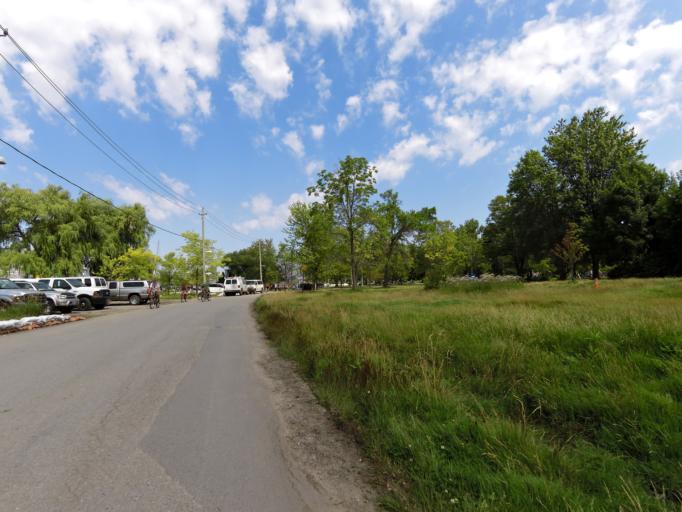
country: CA
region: Ontario
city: Toronto
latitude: 43.6304
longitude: -79.3566
